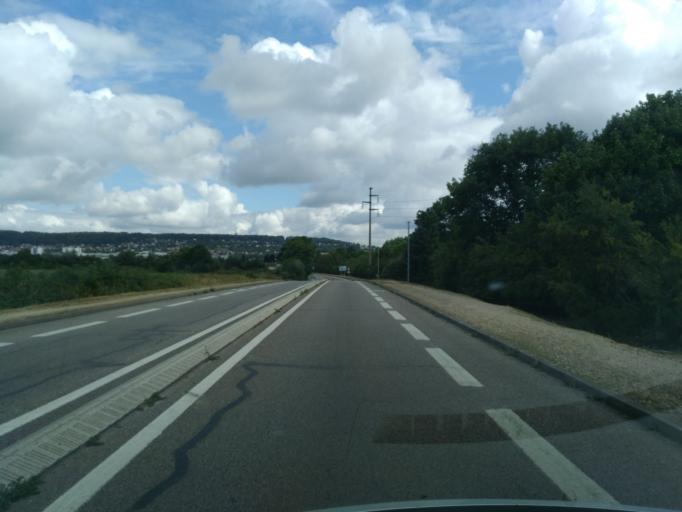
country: FR
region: Ile-de-France
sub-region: Departement des Yvelines
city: Carrieres-sous-Poissy
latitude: 48.9590
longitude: 2.0423
